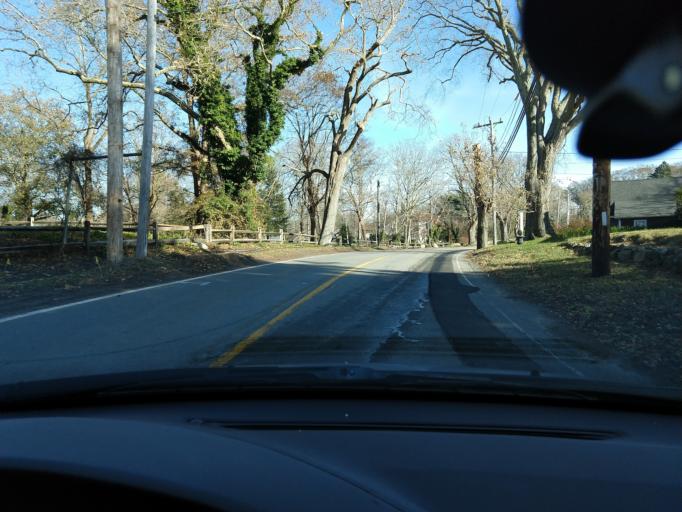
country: US
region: Massachusetts
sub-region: Barnstable County
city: Barnstable
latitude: 41.7044
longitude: -70.3204
